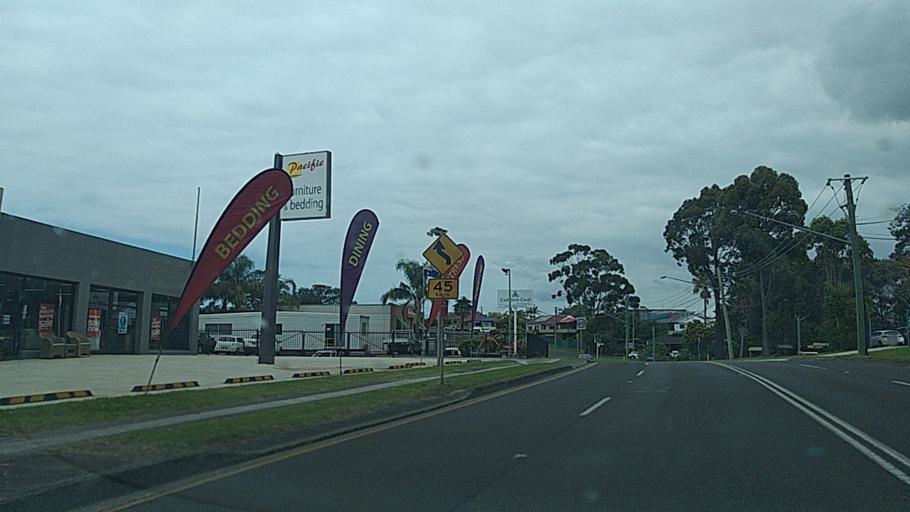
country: AU
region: New South Wales
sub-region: Wollongong
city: Bulli
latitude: -34.3557
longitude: 150.9006
